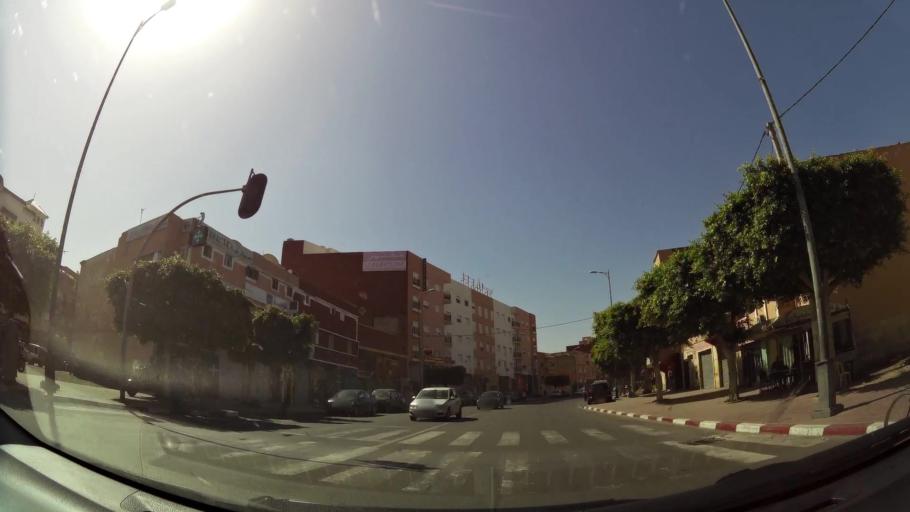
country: MA
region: Souss-Massa-Draa
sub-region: Inezgane-Ait Mellou
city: Inezgane
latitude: 30.3417
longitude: -9.5023
